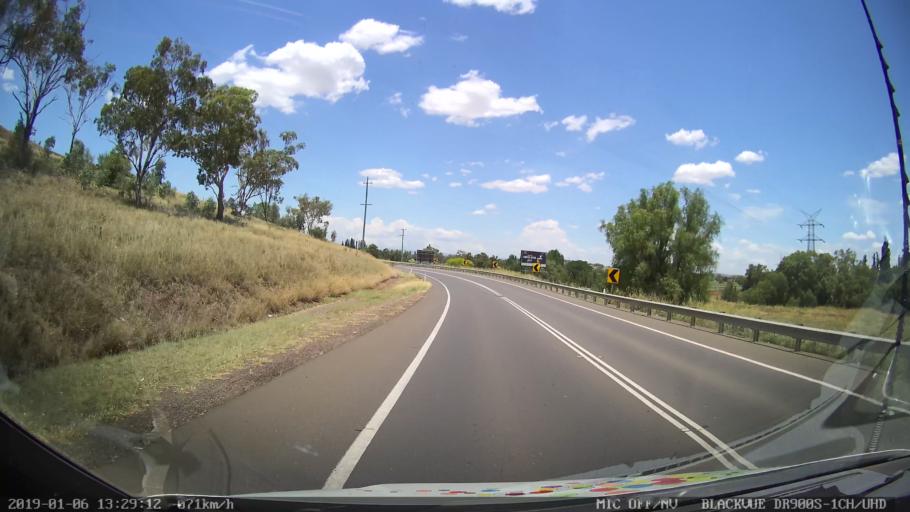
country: AU
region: New South Wales
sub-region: Tamworth Municipality
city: East Tamworth
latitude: -31.1211
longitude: 150.9697
